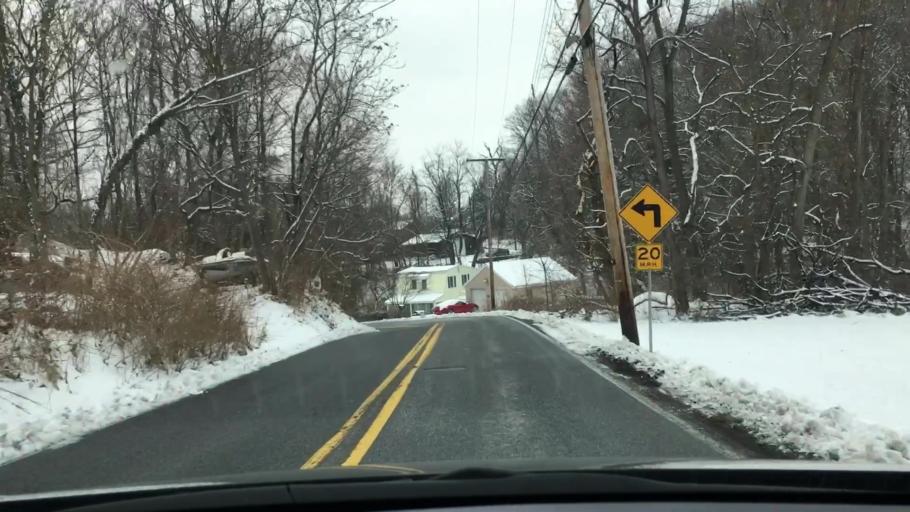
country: US
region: Pennsylvania
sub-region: York County
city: Emigsville
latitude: 40.0058
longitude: -76.7041
